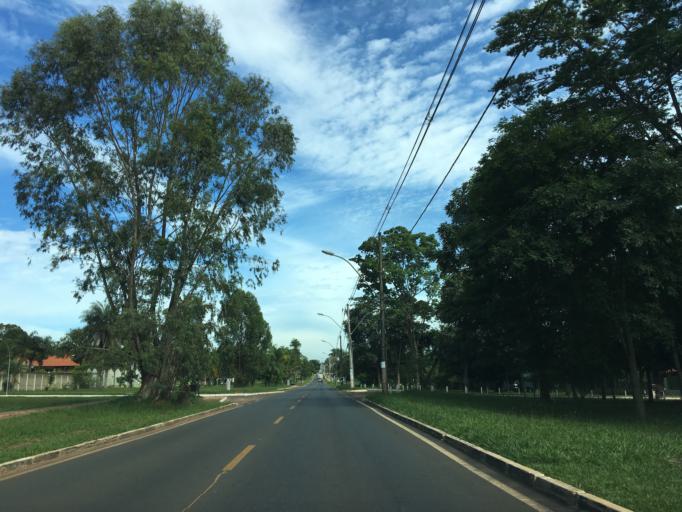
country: BR
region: Federal District
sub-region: Brasilia
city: Brasilia
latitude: -15.8628
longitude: -47.9752
